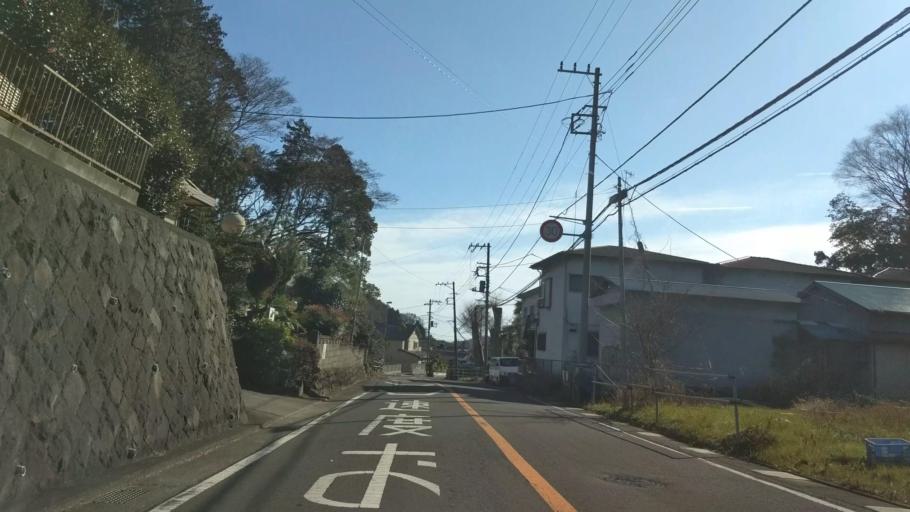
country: JP
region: Kanagawa
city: Ninomiya
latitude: 35.3335
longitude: 139.2331
